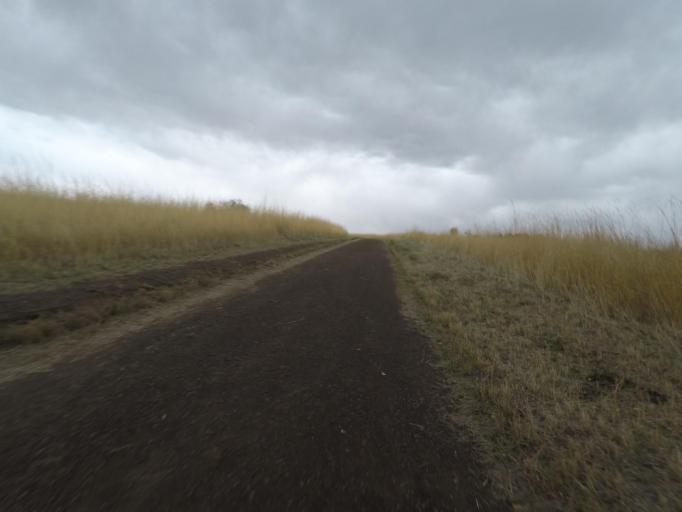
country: US
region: Washington
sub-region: Walla Walla County
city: Walla Walla East
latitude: 46.0725
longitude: -118.2579
